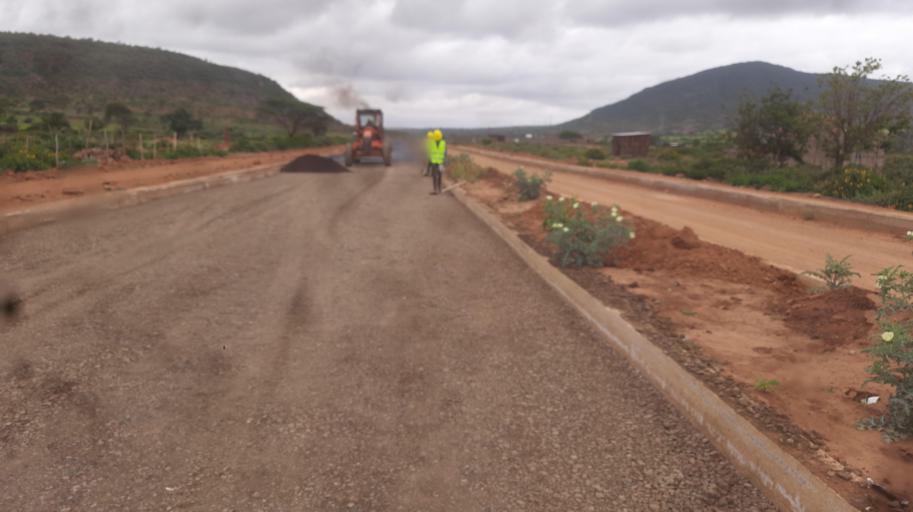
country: ET
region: Oromiya
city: Yabelo
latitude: 4.8905
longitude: 38.1209
